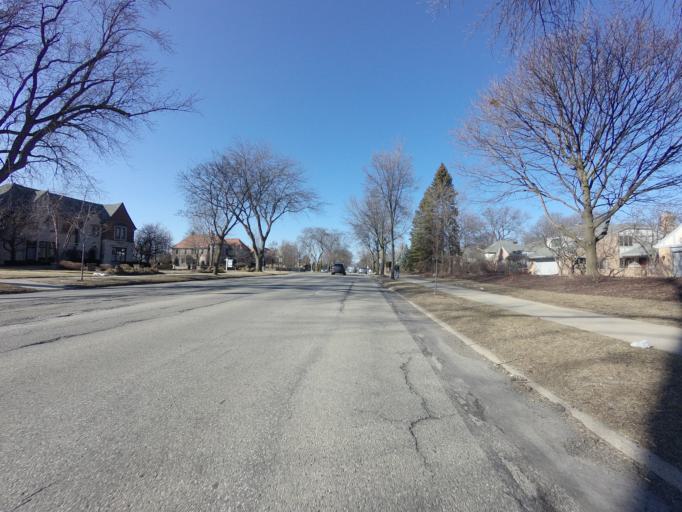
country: US
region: Wisconsin
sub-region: Milwaukee County
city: Shorewood
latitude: 43.0855
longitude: -87.8732
